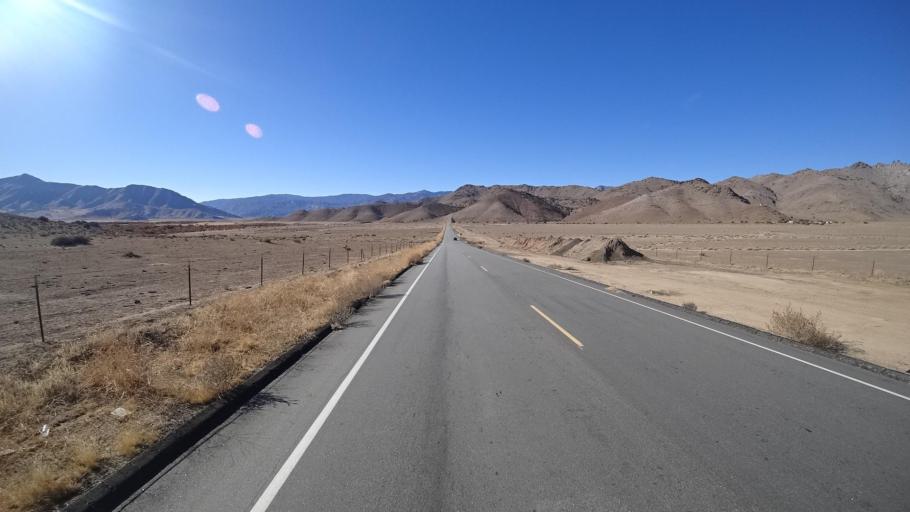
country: US
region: California
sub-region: Kern County
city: Weldon
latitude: 35.6787
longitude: -118.3636
